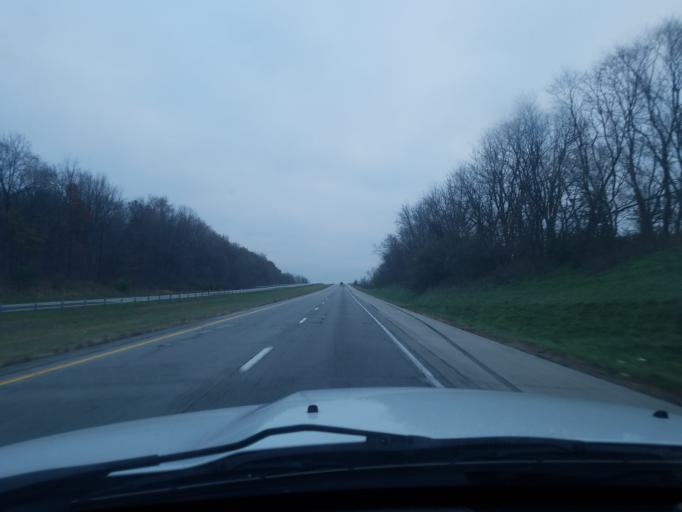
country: US
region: Indiana
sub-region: Madison County
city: Chesterfield
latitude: 40.0649
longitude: -85.5904
